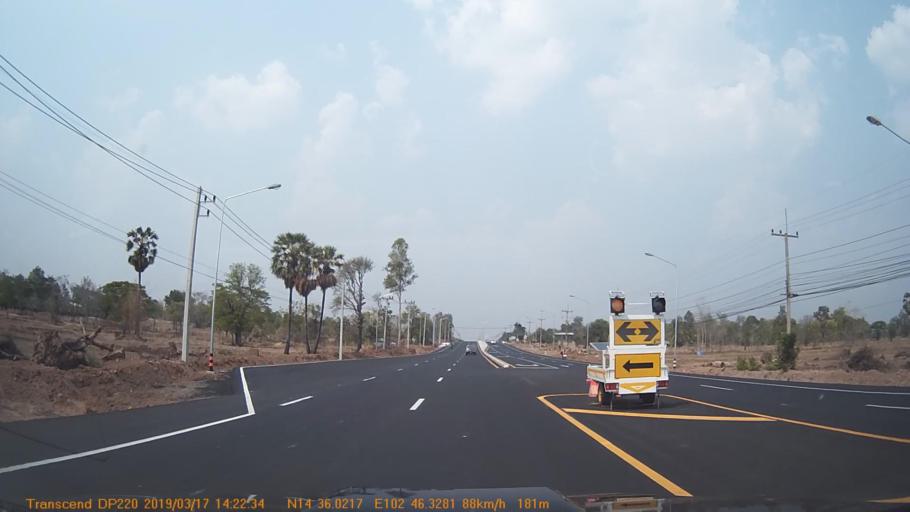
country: TH
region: Buriram
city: Nang Rong
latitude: 14.6007
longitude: 102.7723
